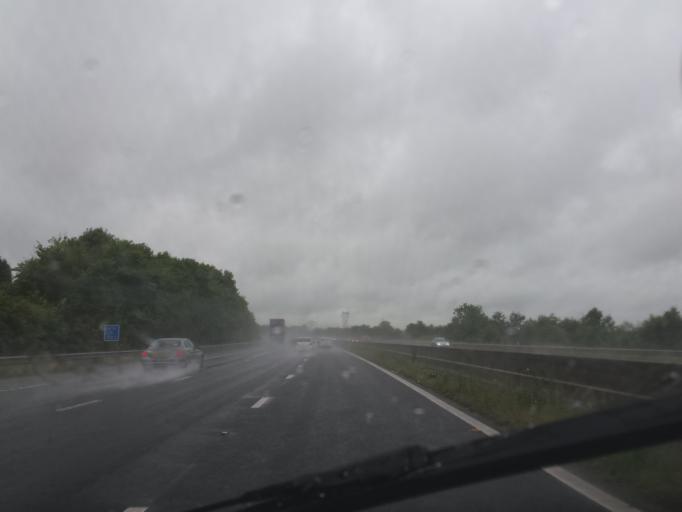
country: GB
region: England
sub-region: Rotherham
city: Hellaby
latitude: 53.4485
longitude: -1.2305
